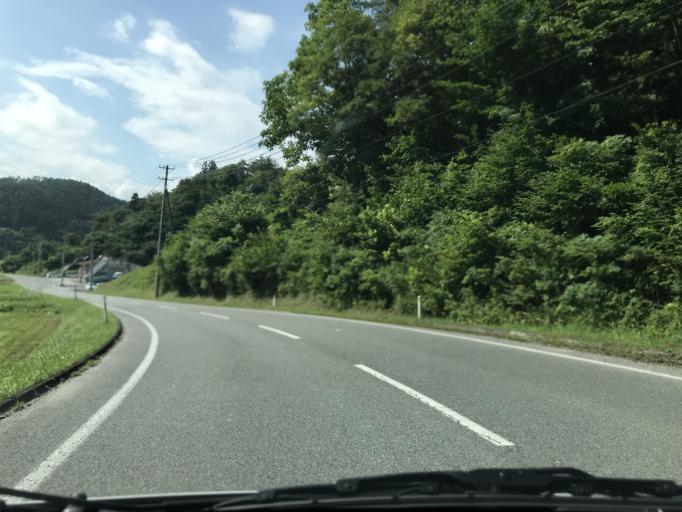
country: JP
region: Iwate
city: Ichinoseki
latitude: 39.0060
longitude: 141.2668
